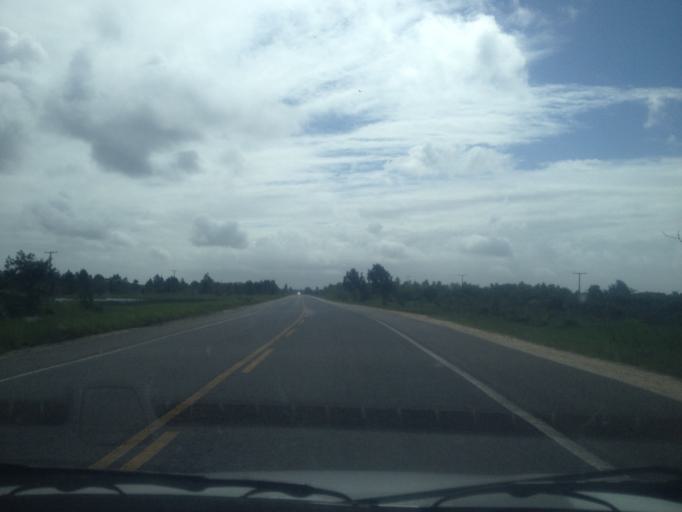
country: BR
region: Bahia
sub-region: Conde
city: Conde
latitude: -11.8635
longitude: -37.6314
